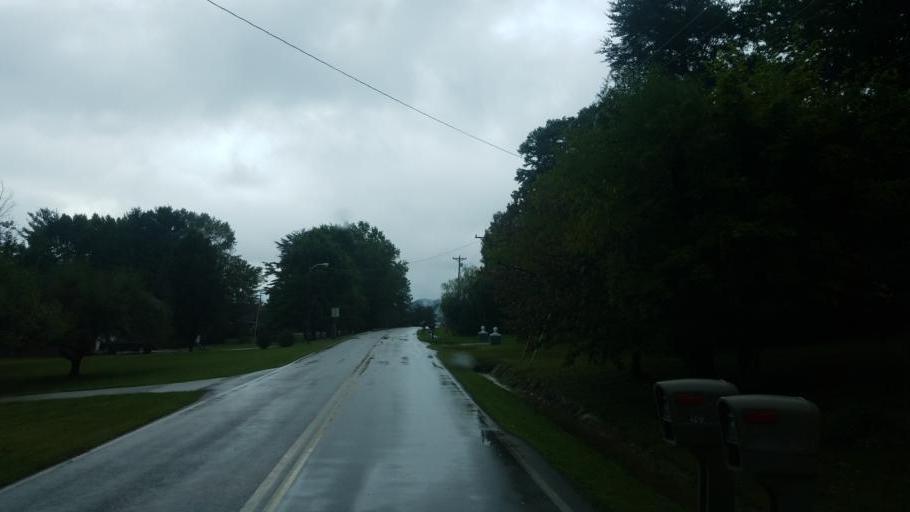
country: US
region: Kentucky
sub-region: Rowan County
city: Morehead
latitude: 38.1837
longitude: -83.4817
